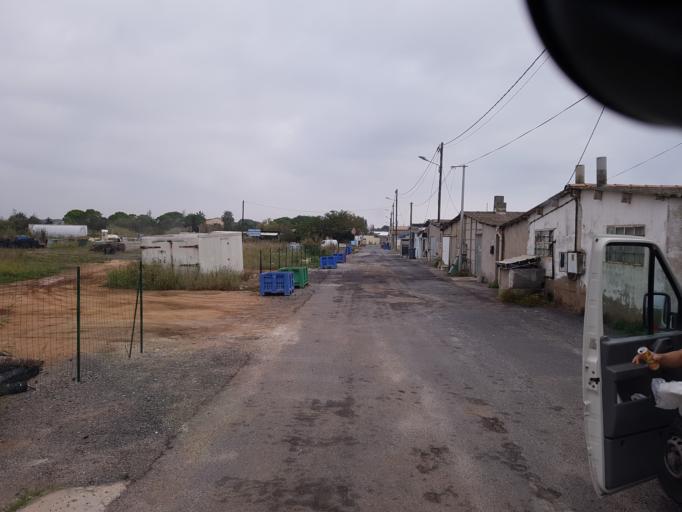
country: FR
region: Languedoc-Roussillon
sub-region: Departement de l'Herault
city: Marseillan
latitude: 43.3626
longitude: 3.5362
